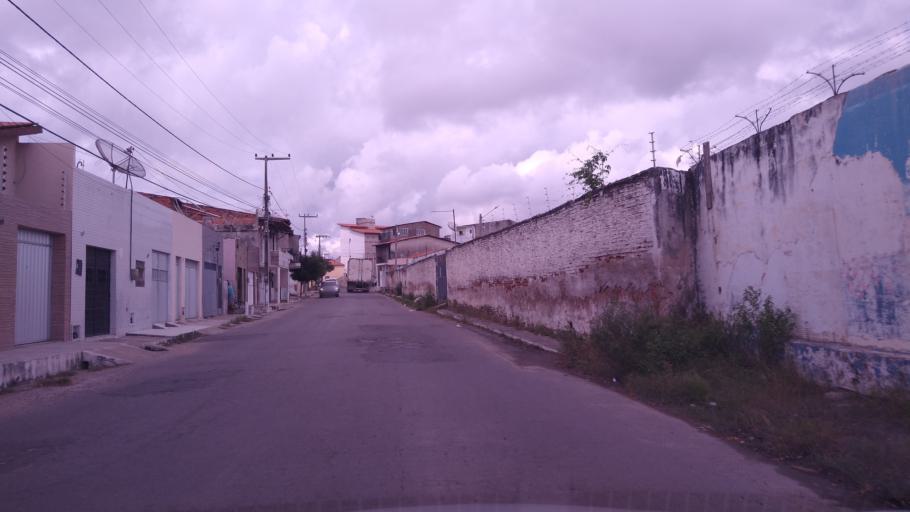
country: BR
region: Ceara
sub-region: Quixada
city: Quixada
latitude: -4.9644
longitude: -39.0148
